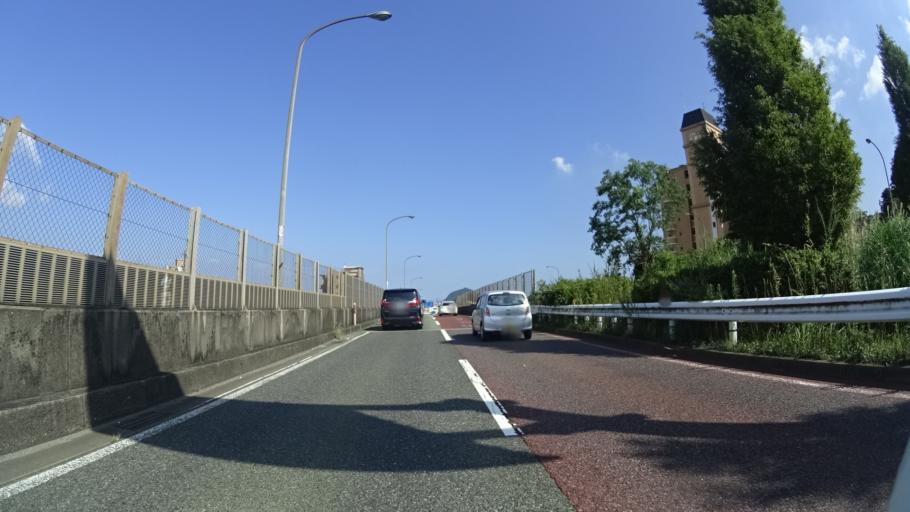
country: JP
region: Fukuoka
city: Kanda
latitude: 33.8107
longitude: 130.9513
